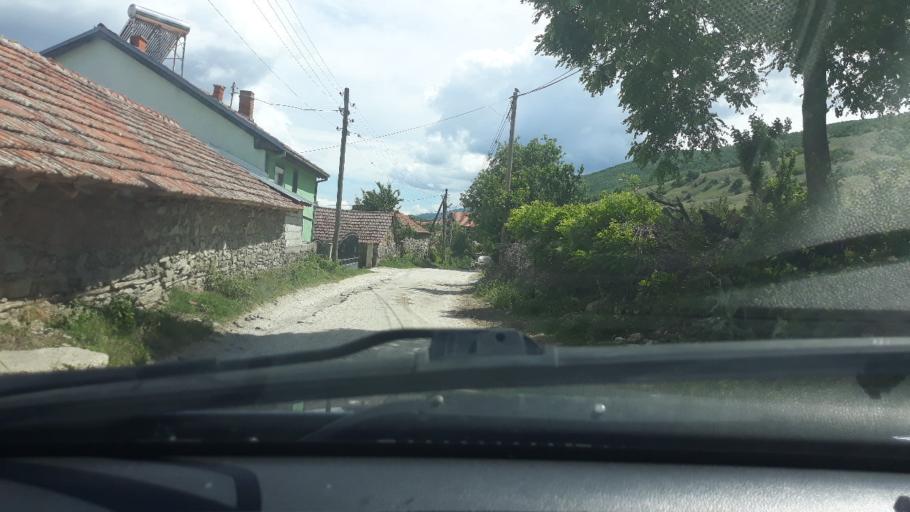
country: MK
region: Krivogastani
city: Krivogashtani
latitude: 41.3231
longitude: 21.3045
